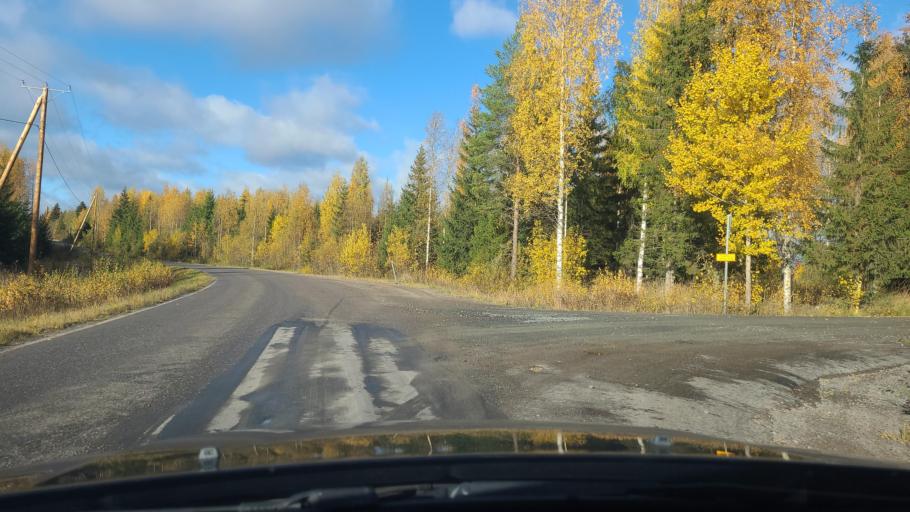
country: FI
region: Southern Savonia
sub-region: Pieksaemaeki
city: Juva
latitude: 61.8824
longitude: 27.7535
